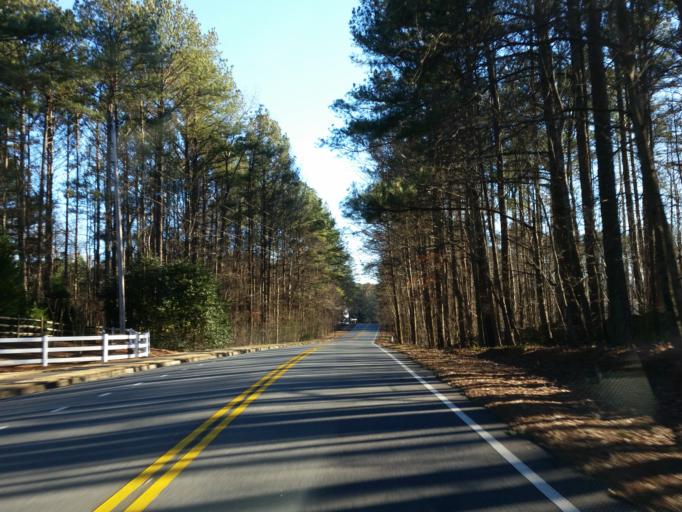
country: US
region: Georgia
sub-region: Cobb County
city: Kennesaw
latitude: 33.9802
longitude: -84.6902
